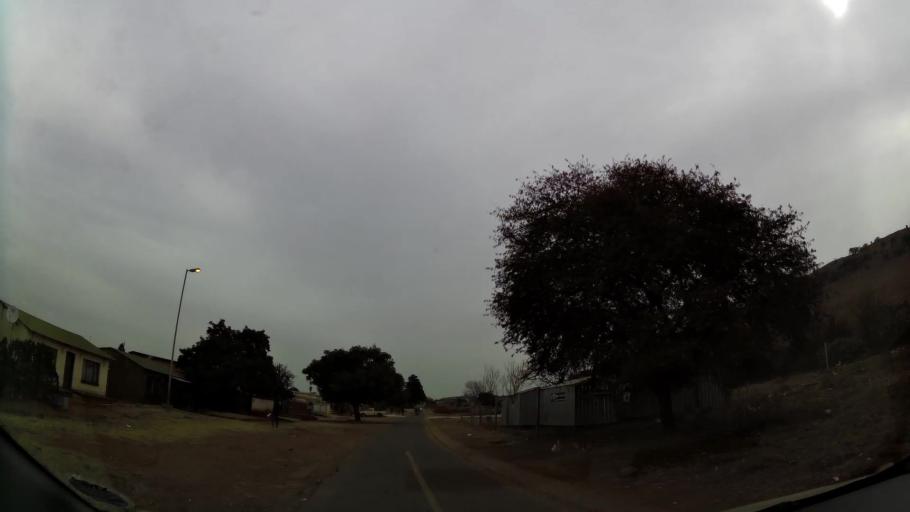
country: ZA
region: Gauteng
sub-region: City of Tshwane Metropolitan Municipality
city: Pretoria
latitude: -25.7013
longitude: 28.3360
